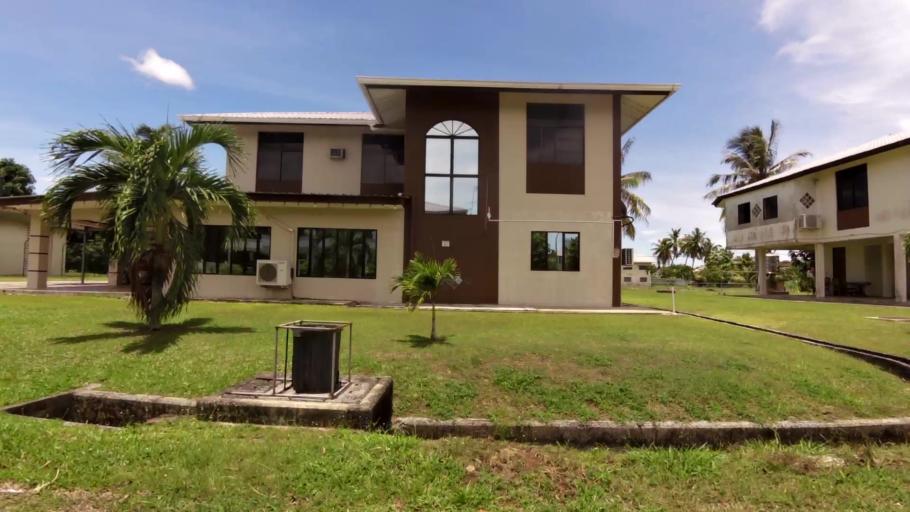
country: BN
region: Belait
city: Kuala Belait
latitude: 4.5833
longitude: 114.2373
